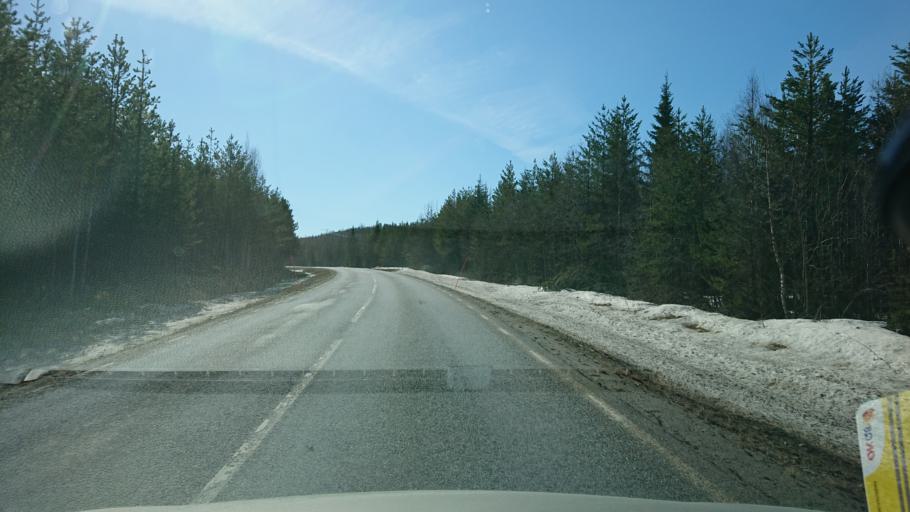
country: SE
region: Vaesterbotten
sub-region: Dorotea Kommun
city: Dorotea
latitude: 63.9999
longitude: 16.3048
